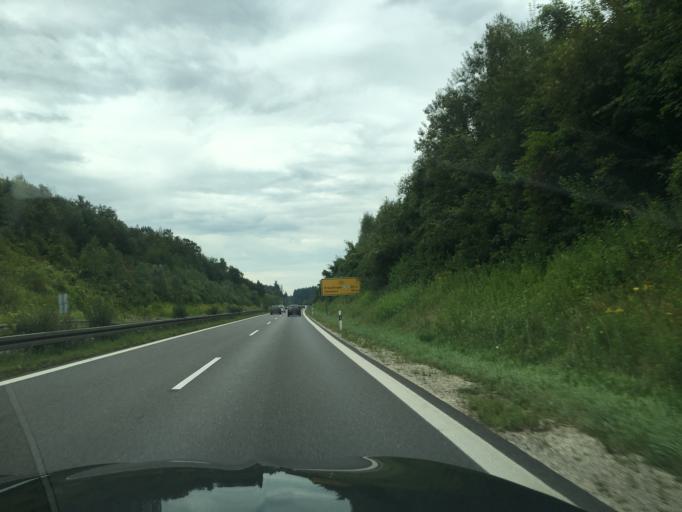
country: DE
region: Baden-Wuerttemberg
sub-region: Freiburg Region
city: Radolfzell am Bodensee
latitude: 47.7606
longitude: 8.9887
